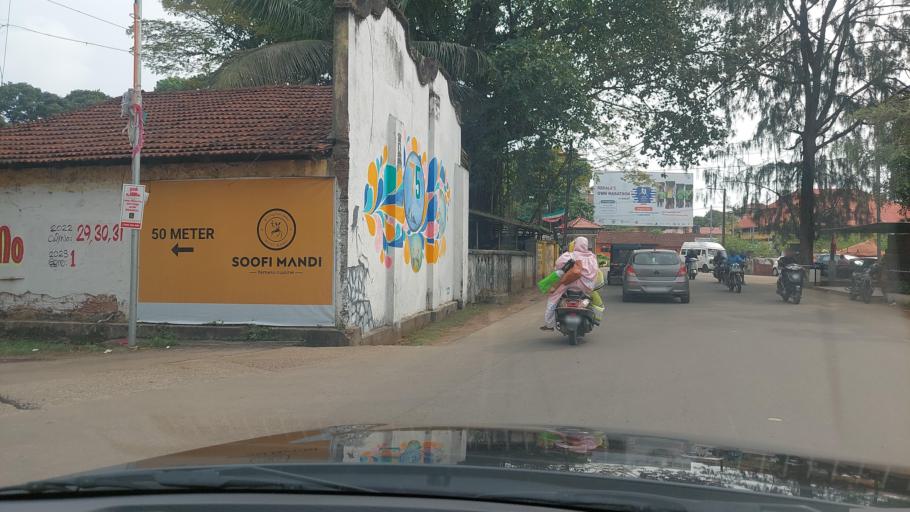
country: IN
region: Kerala
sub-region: Kozhikode
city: Kozhikode
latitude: 11.2551
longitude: 75.7725
